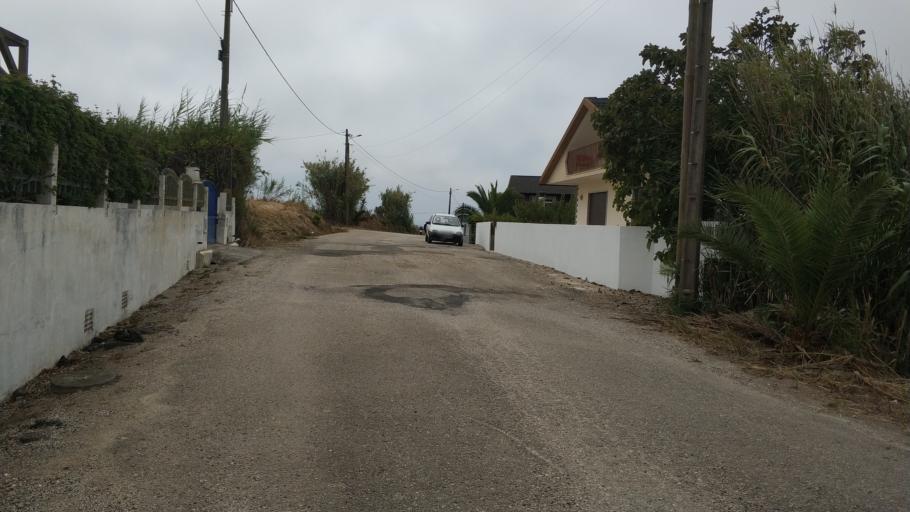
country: PT
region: Lisbon
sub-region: Lourinha
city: Lourinha
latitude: 39.2111
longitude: -9.3212
